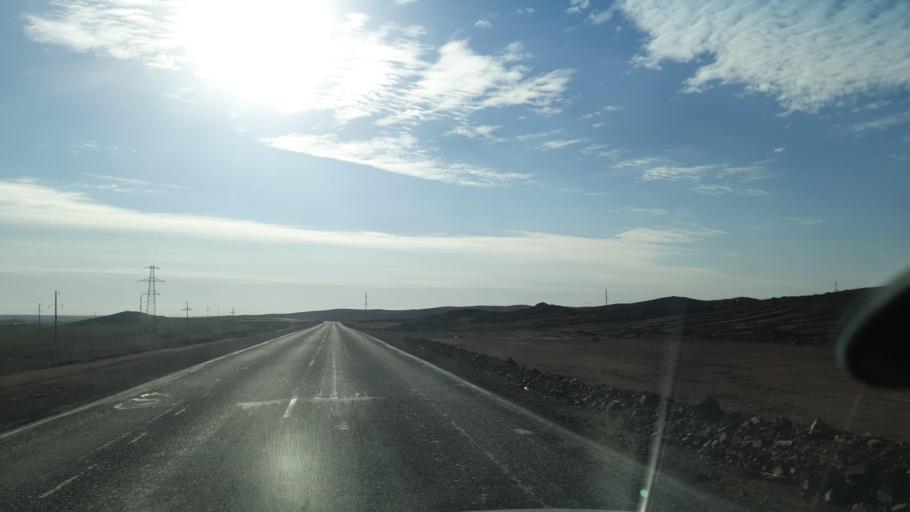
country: KZ
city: Priozersk
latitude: 45.8052
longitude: 73.3927
